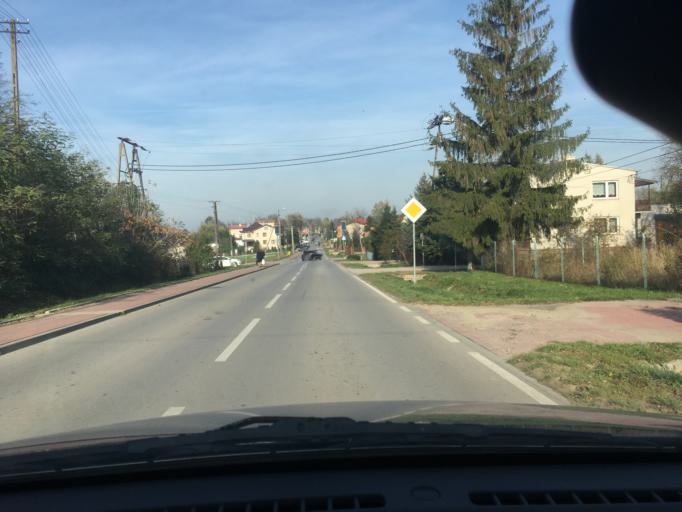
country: PL
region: Masovian Voivodeship
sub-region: Powiat plocki
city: Bodzanow
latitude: 52.4949
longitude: 20.0308
